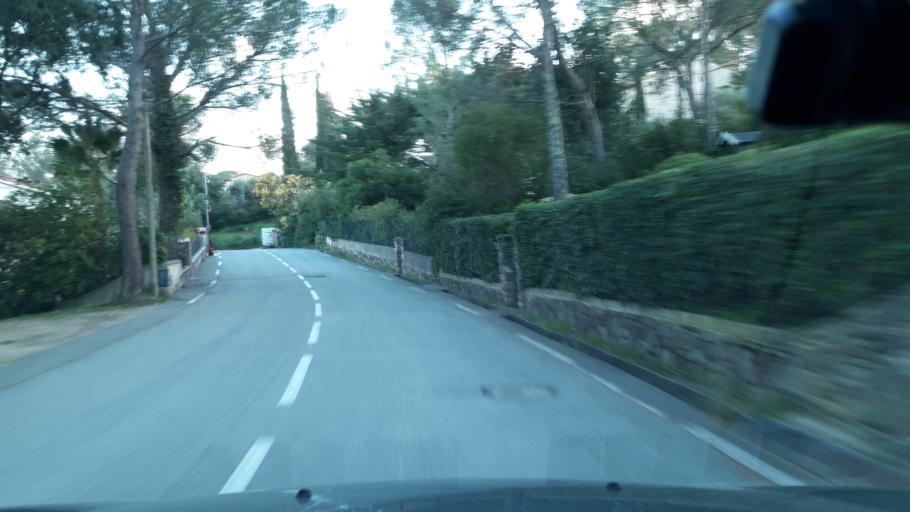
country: FR
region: Provence-Alpes-Cote d'Azur
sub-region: Departement du Var
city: Saint-Raphael
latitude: 43.4611
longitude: 6.7683
